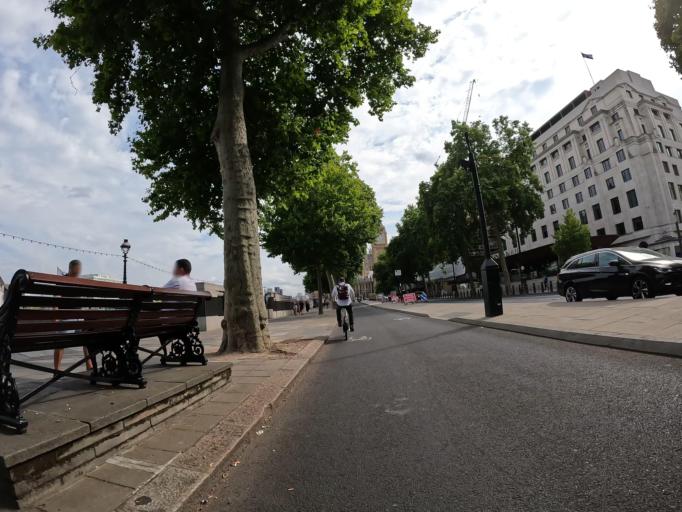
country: GB
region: England
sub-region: Greater London
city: Bromley
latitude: 51.4015
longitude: 0.0300
